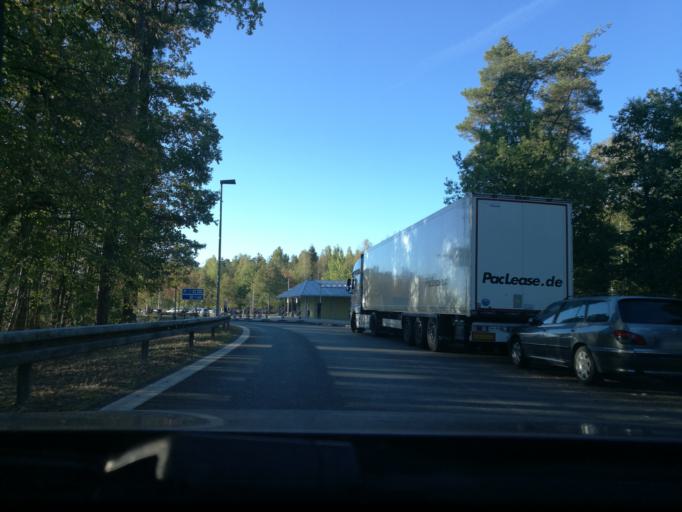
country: DE
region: Bavaria
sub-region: Regierungsbezirk Mittelfranken
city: Wetzendorf
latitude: 49.5262
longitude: 11.0687
